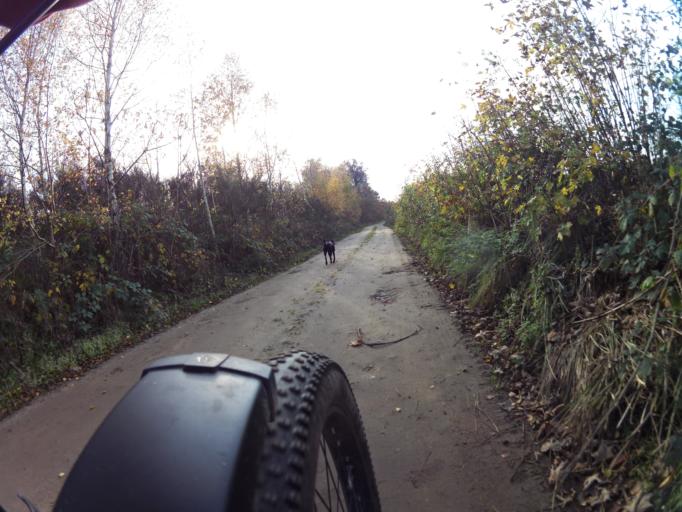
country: PL
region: Pomeranian Voivodeship
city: Strzelno
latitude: 54.7469
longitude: 18.2873
